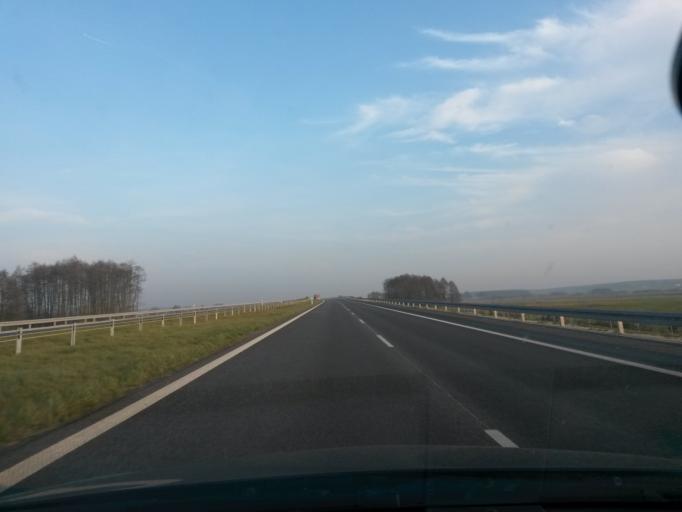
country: PL
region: Greater Poland Voivodeship
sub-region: Powiat kepinski
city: Bralin
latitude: 51.2996
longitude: 17.8904
